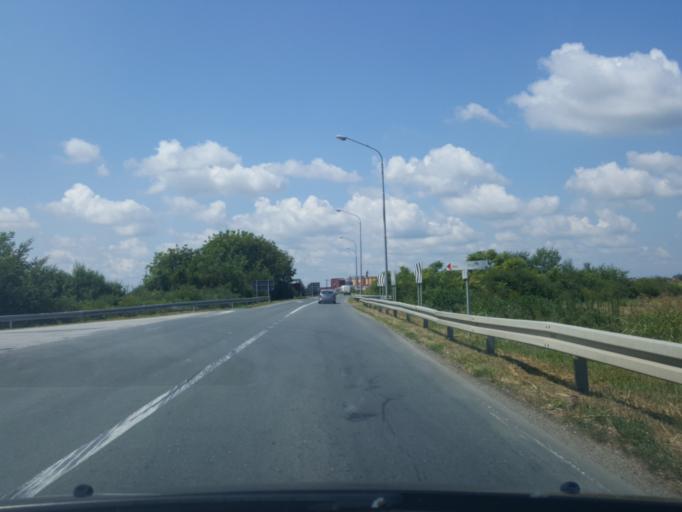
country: RS
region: Autonomna Pokrajina Vojvodina
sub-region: Sremski Okrug
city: Sremska Mitrovica
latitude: 44.9513
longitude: 19.6231
